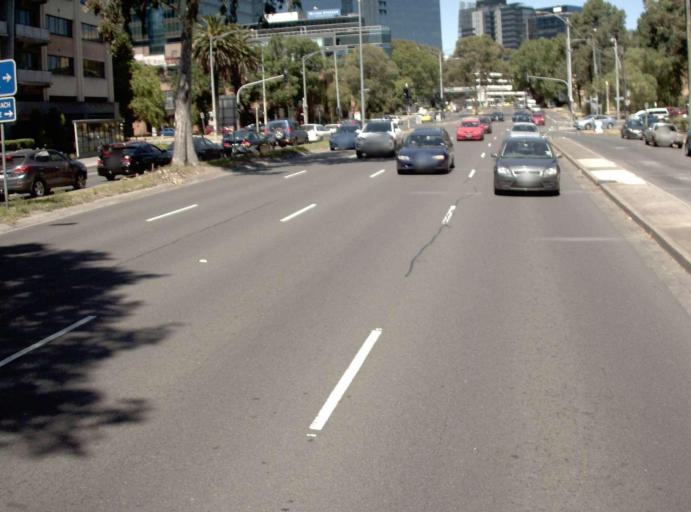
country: AU
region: Victoria
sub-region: Port Phillip
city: South Melbourne
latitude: -37.8347
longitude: 144.9700
